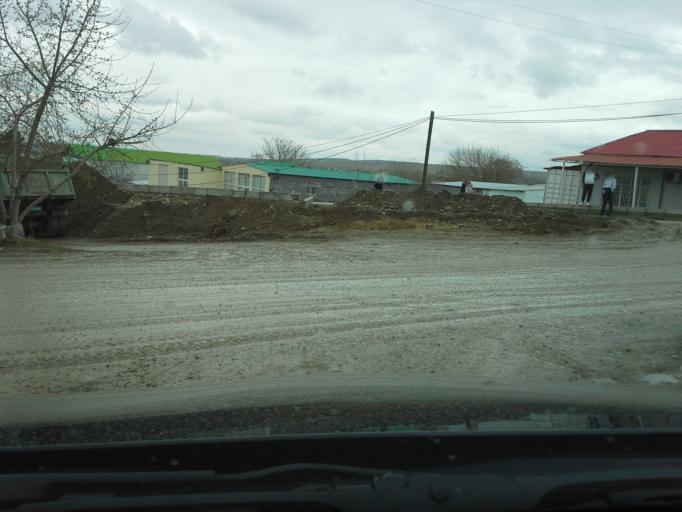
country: TM
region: Ahal
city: Abadan
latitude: 37.9621
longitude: 58.2113
